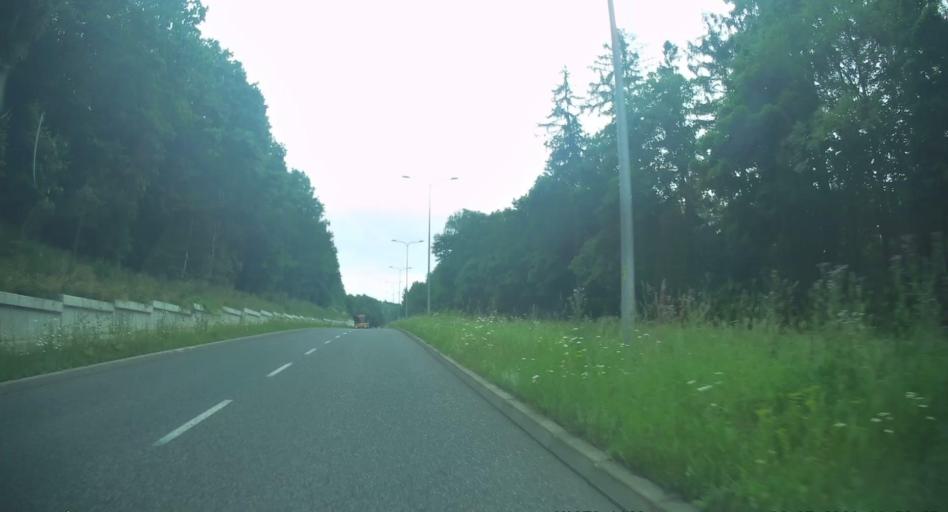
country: PL
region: Lower Silesian Voivodeship
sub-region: Powiat walbrzyski
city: Walbrzych
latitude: 50.7654
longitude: 16.3169
